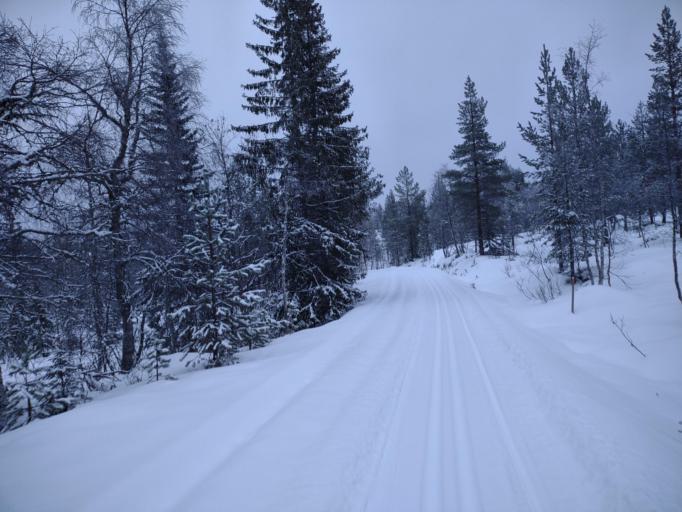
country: NO
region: Buskerud
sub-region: Flesberg
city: Lampeland
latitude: 59.7466
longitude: 9.4909
